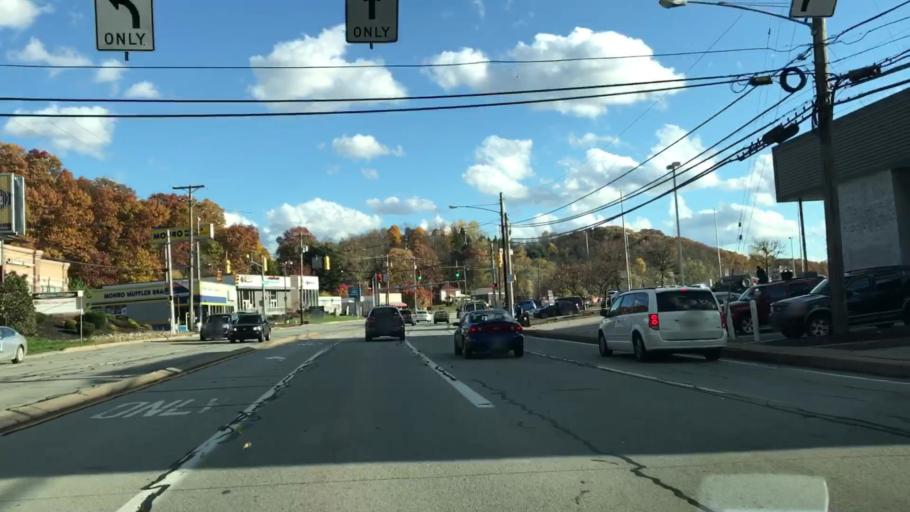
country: US
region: Pennsylvania
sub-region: Allegheny County
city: West View
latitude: 40.5287
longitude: -80.0077
